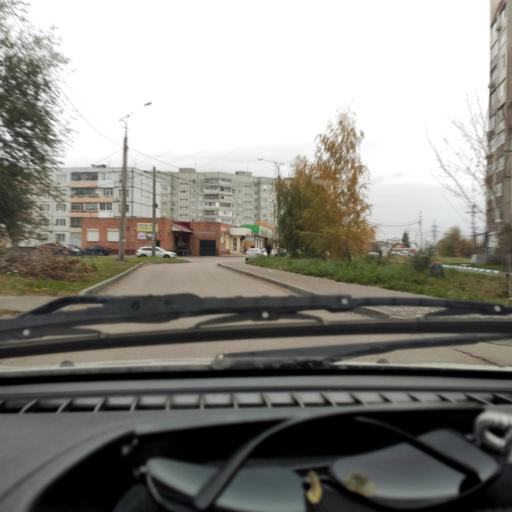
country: RU
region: Samara
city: Tol'yatti
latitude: 53.5398
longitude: 49.3965
